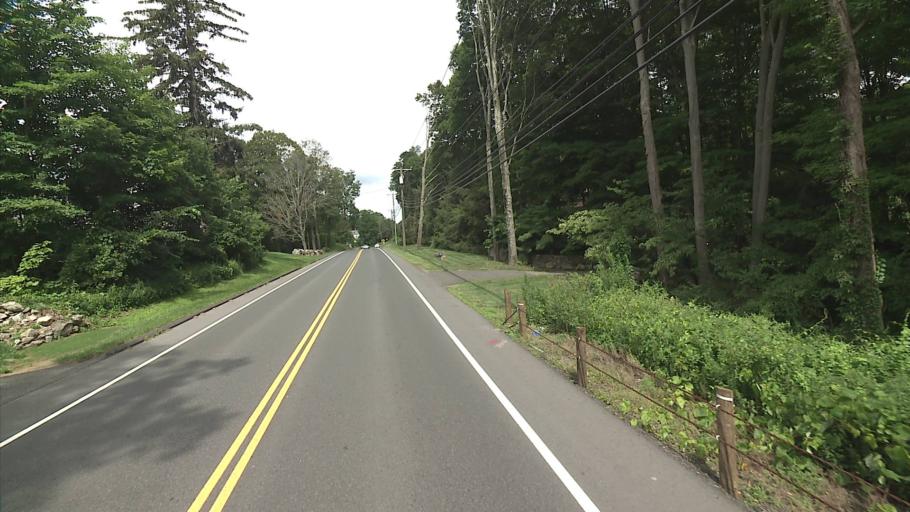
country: US
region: Connecticut
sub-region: New Haven County
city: Southbury
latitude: 41.4684
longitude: -73.1755
